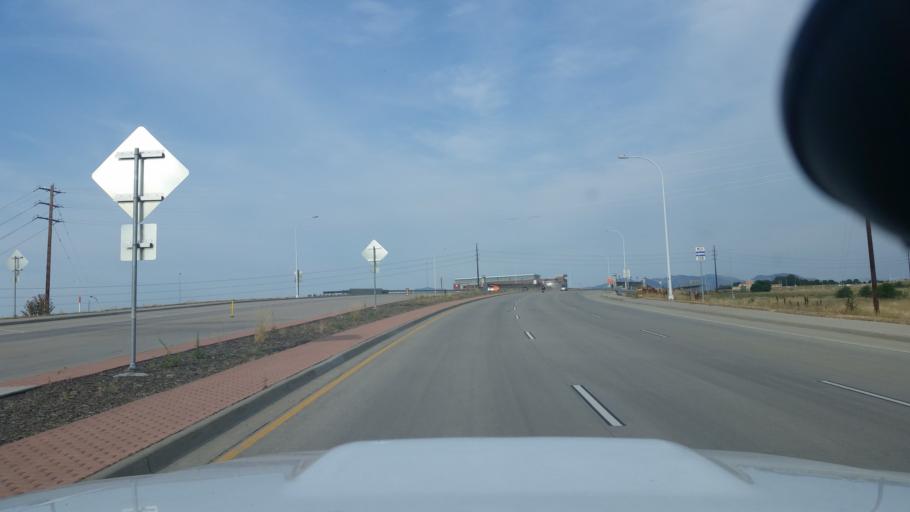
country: US
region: Colorado
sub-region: Broomfield County
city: Broomfield
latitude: 39.9120
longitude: -105.0851
